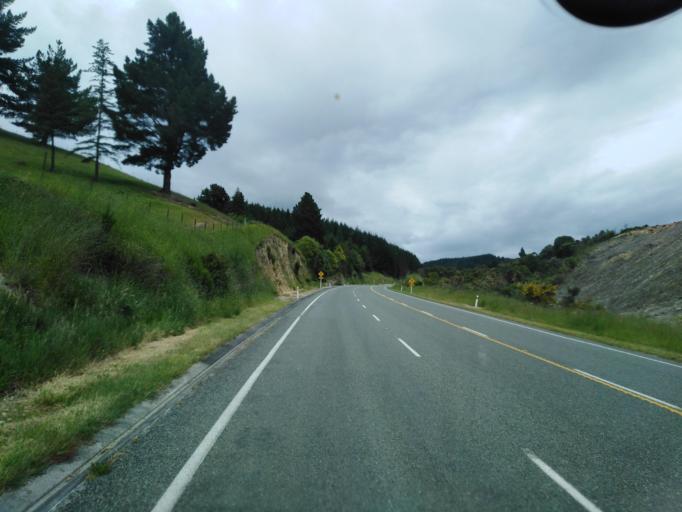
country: NZ
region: Tasman
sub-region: Tasman District
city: Wakefield
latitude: -41.4714
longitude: 172.9409
